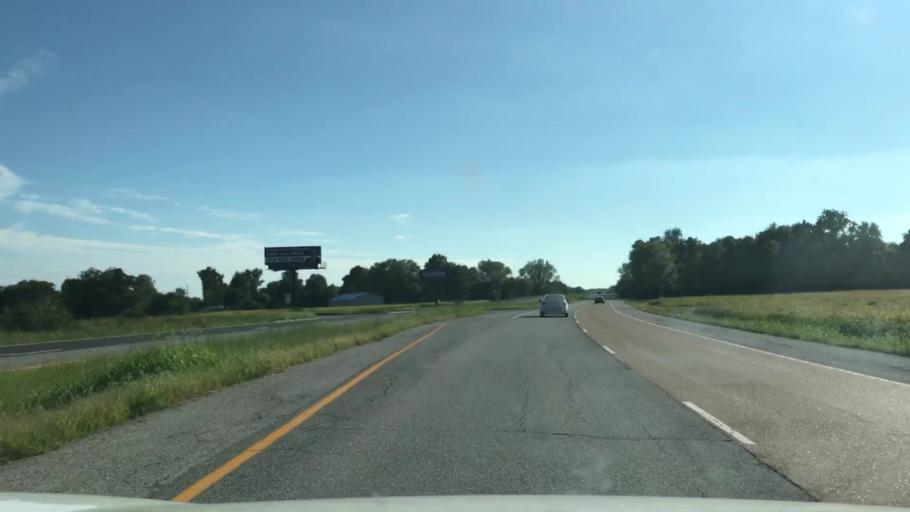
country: US
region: Illinois
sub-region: Madison County
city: Mitchell
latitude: 38.7807
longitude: -90.1101
